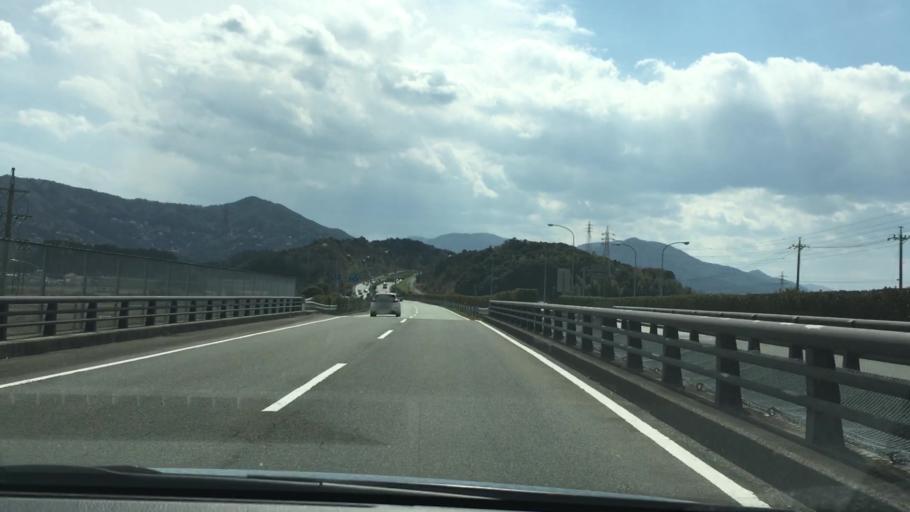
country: JP
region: Mie
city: Ise
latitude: 34.4862
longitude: 136.7553
